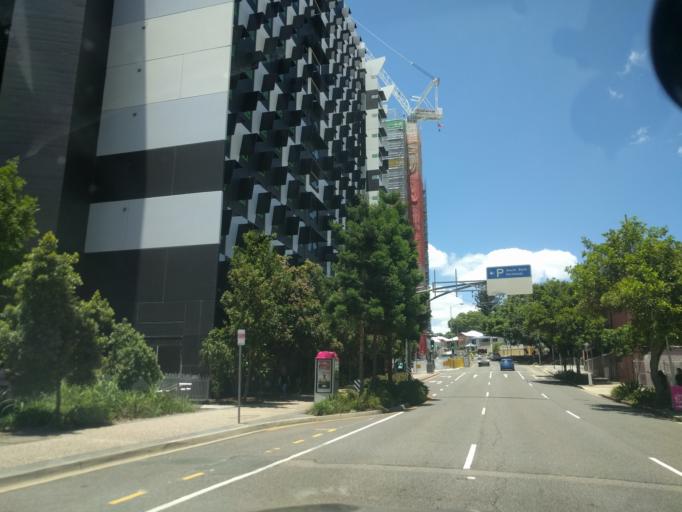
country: AU
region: Queensland
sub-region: Brisbane
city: South Brisbane
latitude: -27.4812
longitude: 153.0208
